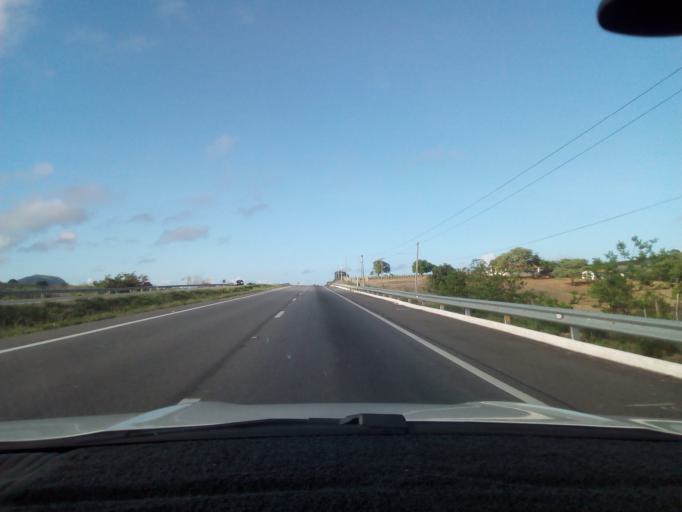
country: BR
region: Paraiba
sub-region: Inga
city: Inga
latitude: -7.2269
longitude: -35.5989
